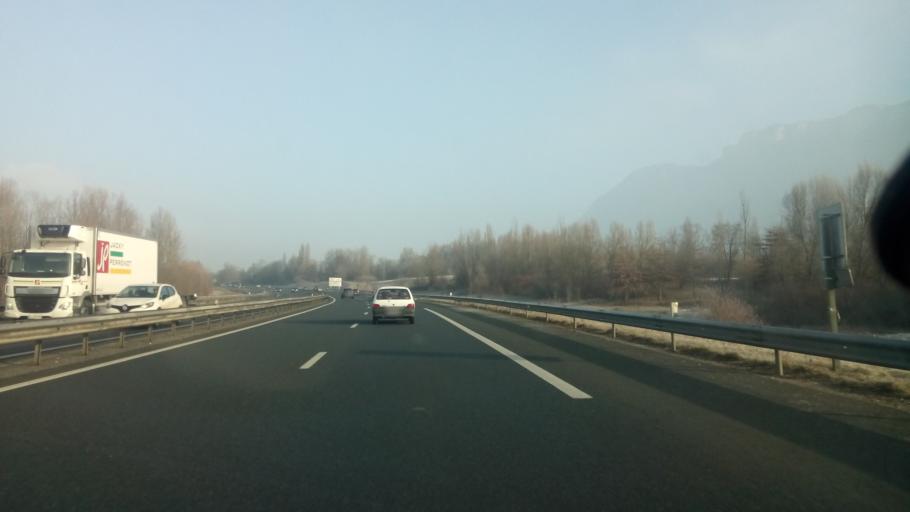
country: FR
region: Rhone-Alpes
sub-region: Departement de la Savoie
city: Sonnaz
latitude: 45.6368
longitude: 5.9193
